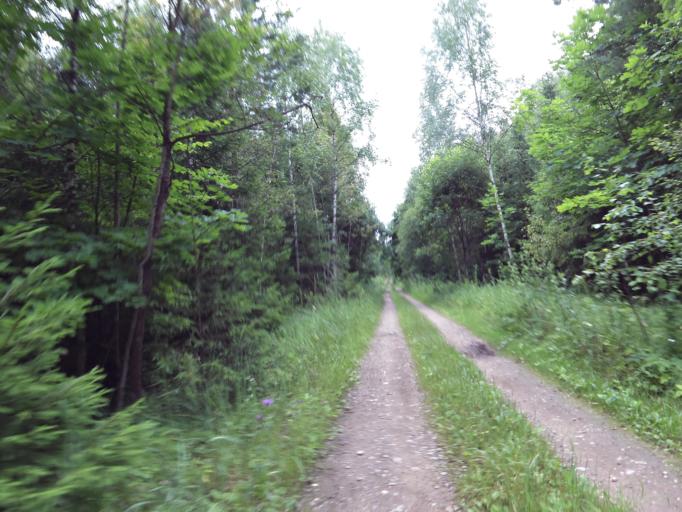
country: RU
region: Moskovskaya
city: Popovo
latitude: 54.9626
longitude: 37.7011
